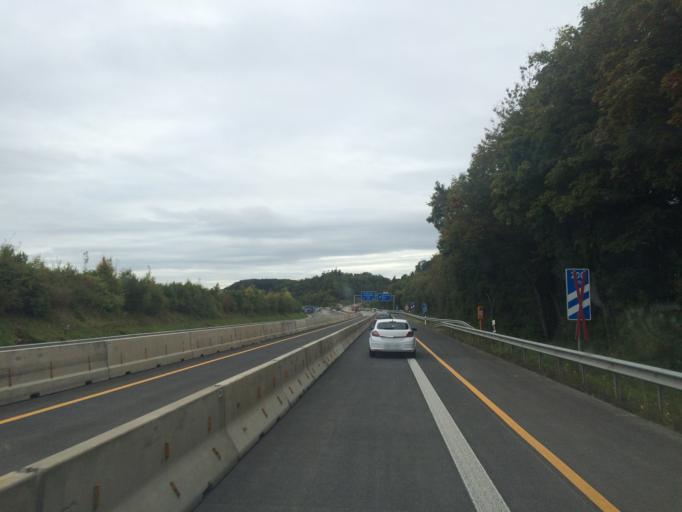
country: DE
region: Rheinland-Pfalz
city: Steiningen
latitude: 50.1898
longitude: 6.9136
